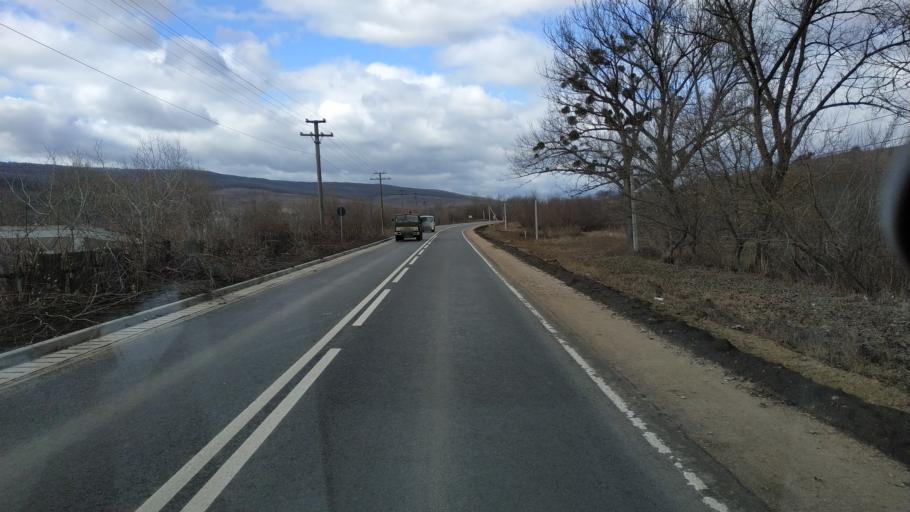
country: MD
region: Stinga Nistrului
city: Bucovat
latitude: 47.1902
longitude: 28.4462
